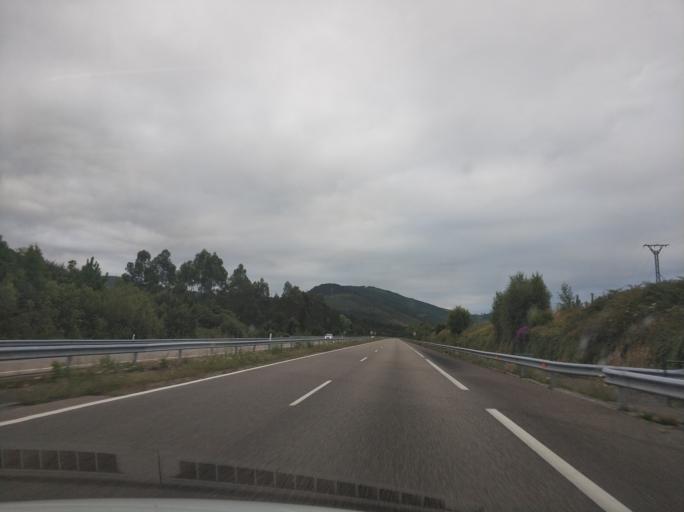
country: ES
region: Asturias
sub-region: Province of Asturias
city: Tineo
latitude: 43.5438
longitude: -6.4726
